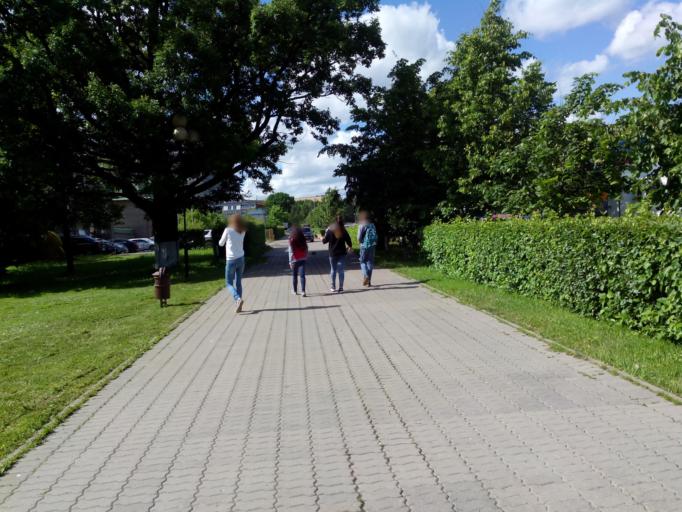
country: RU
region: Moskovskaya
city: Odintsovo
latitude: 55.6793
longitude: 37.2737
